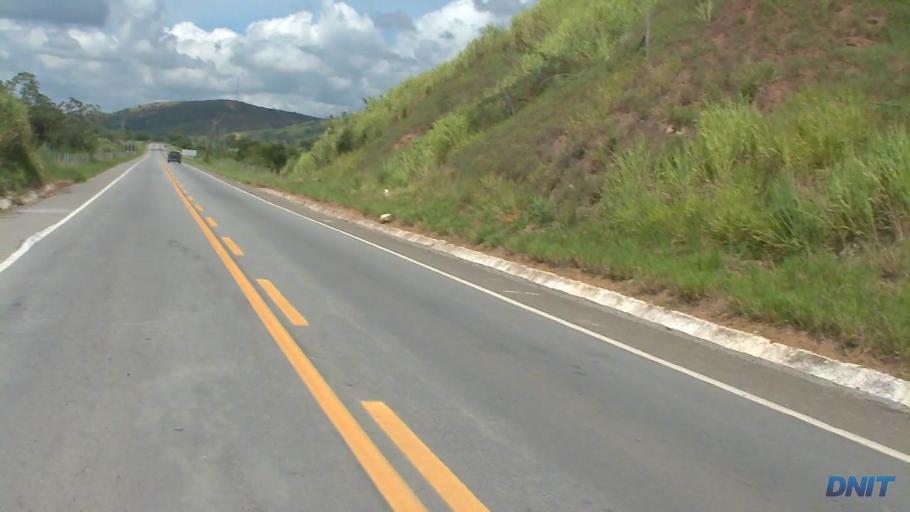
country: BR
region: Minas Gerais
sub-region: Governador Valadares
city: Governador Valadares
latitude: -19.0067
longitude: -42.1327
